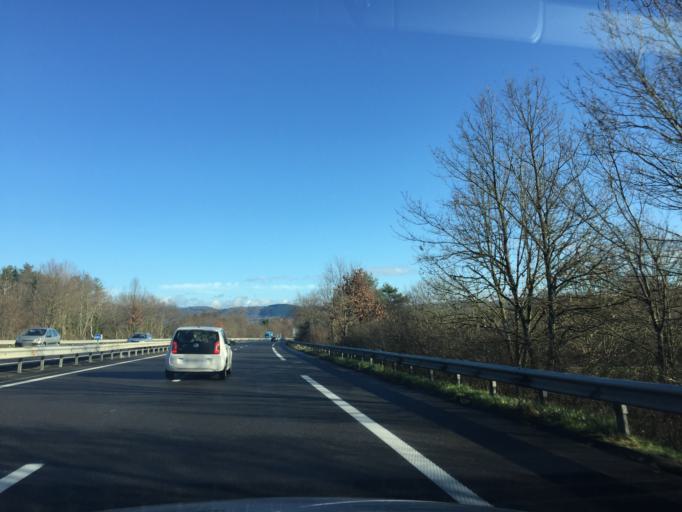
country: FR
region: Auvergne
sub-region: Departement du Puy-de-Dome
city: Orleat
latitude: 45.8539
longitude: 3.4582
